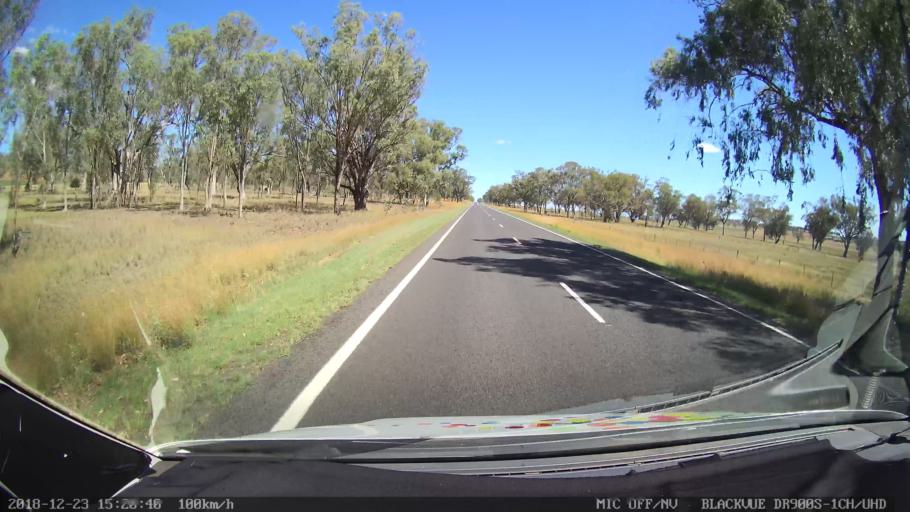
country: AU
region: New South Wales
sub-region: Tamworth Municipality
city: Manilla
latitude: -30.8458
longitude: 150.7913
